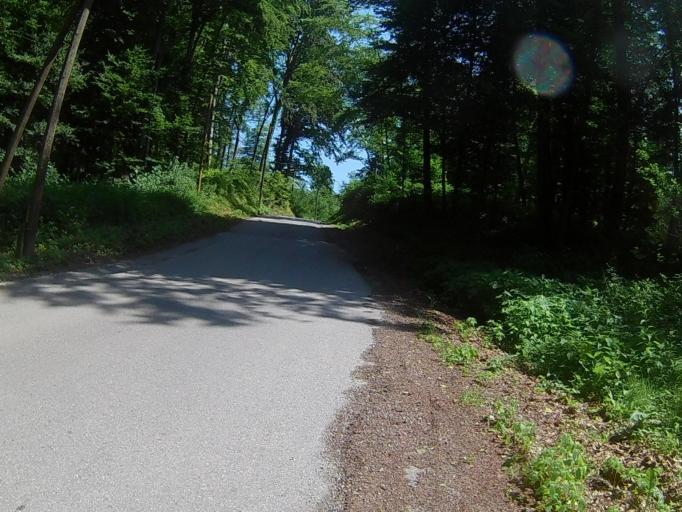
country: SI
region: Maribor
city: Maribor
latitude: 46.5638
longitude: 15.6895
